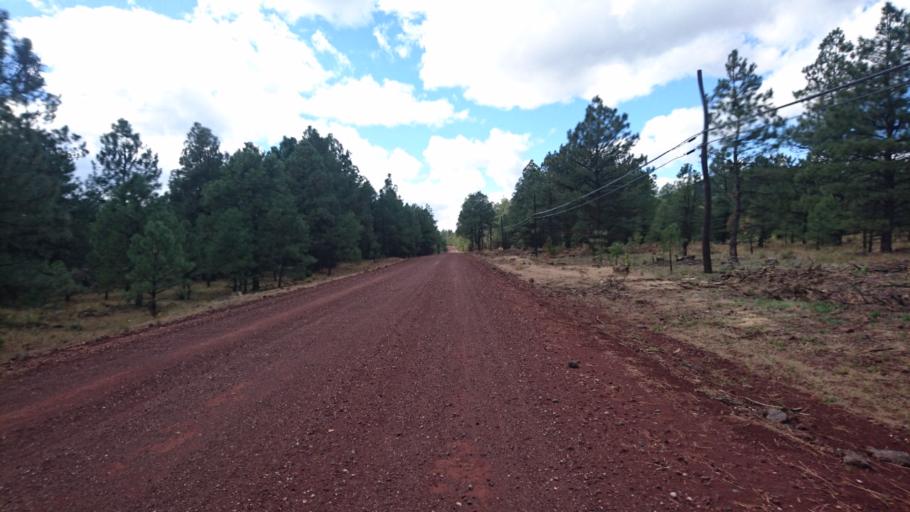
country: US
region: Arizona
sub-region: Coconino County
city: Williams
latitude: 35.2633
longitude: -112.0976
